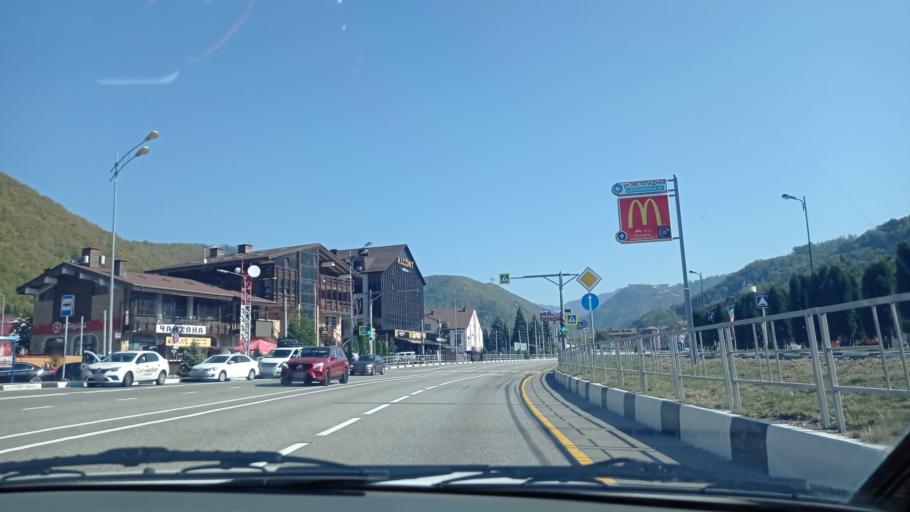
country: RU
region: Krasnodarskiy
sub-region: Sochi City
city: Krasnaya Polyana
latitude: 43.6866
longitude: 40.2506
